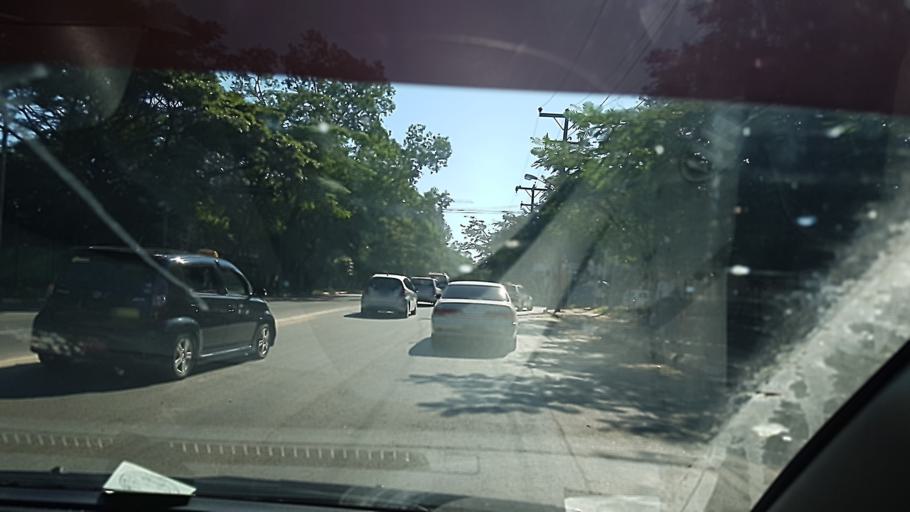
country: MM
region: Yangon
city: Yangon
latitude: 16.8573
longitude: 96.1300
